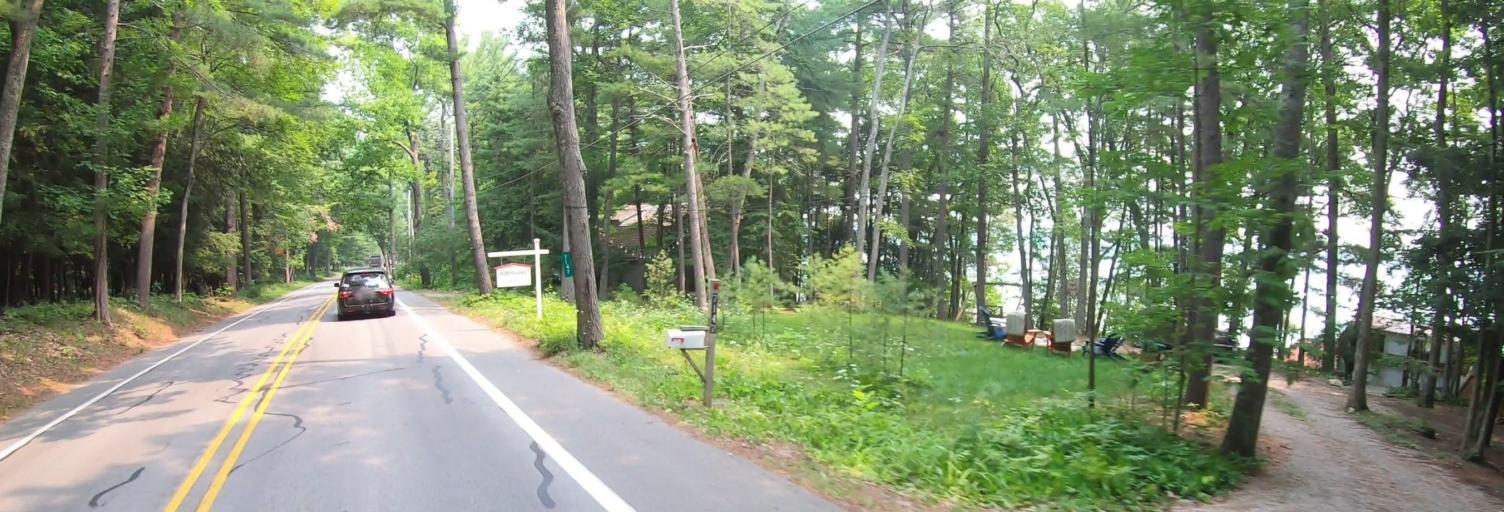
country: US
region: Michigan
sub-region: Benzie County
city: Beulah
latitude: 44.8789
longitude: -85.9910
